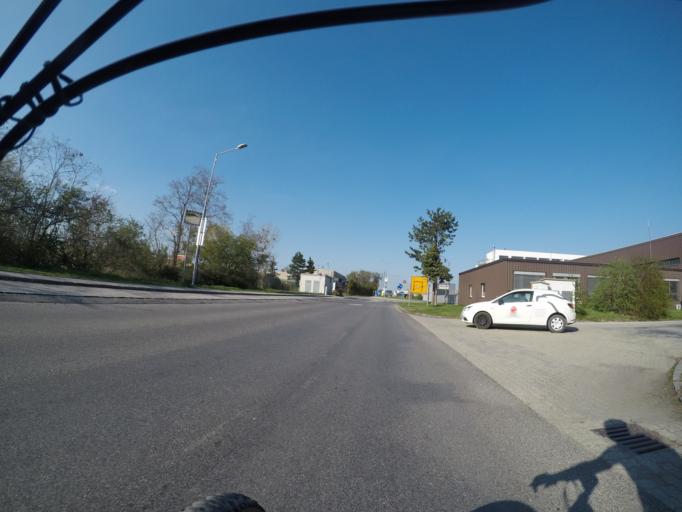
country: AT
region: Lower Austria
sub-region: Politischer Bezirk Modling
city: Wiener Neudorf
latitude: 48.0753
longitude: 16.3168
